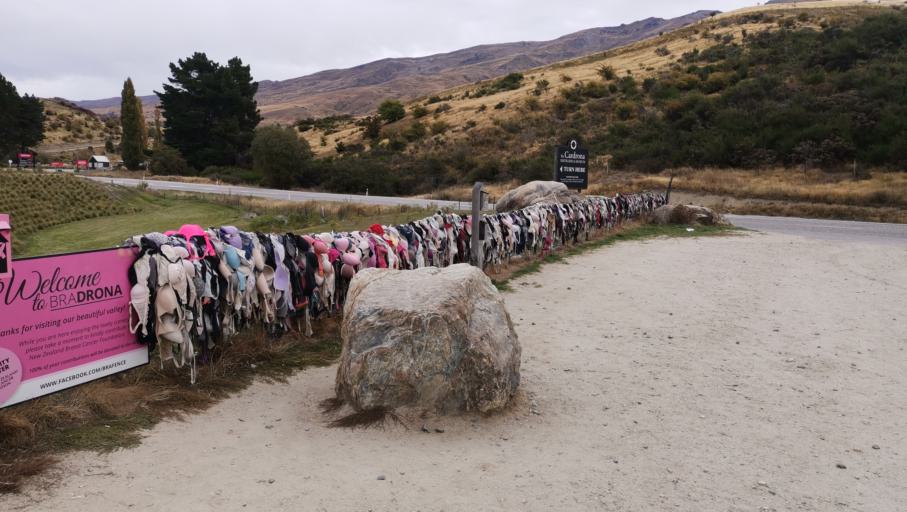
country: NZ
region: Otago
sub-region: Queenstown-Lakes District
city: Wanaka
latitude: -44.8635
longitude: 169.0189
